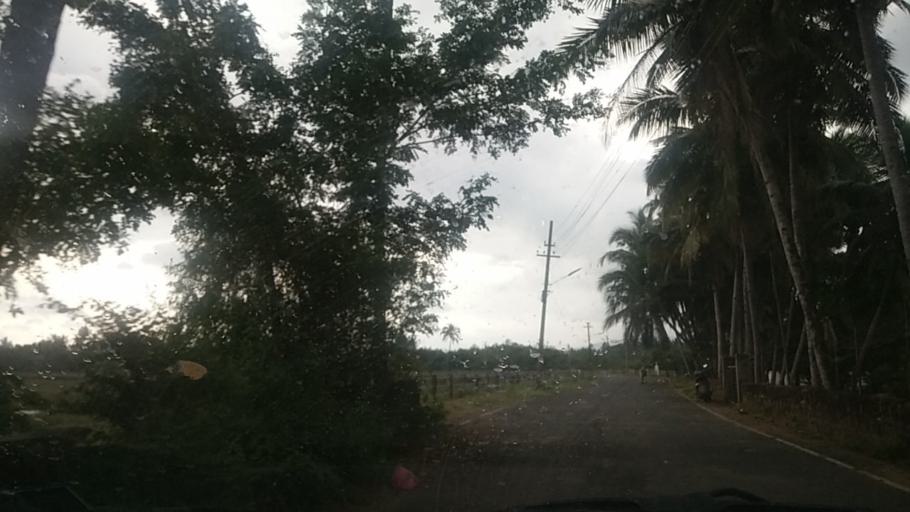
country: IN
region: Goa
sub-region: South Goa
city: Cuncolim
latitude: 15.1942
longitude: 73.9814
